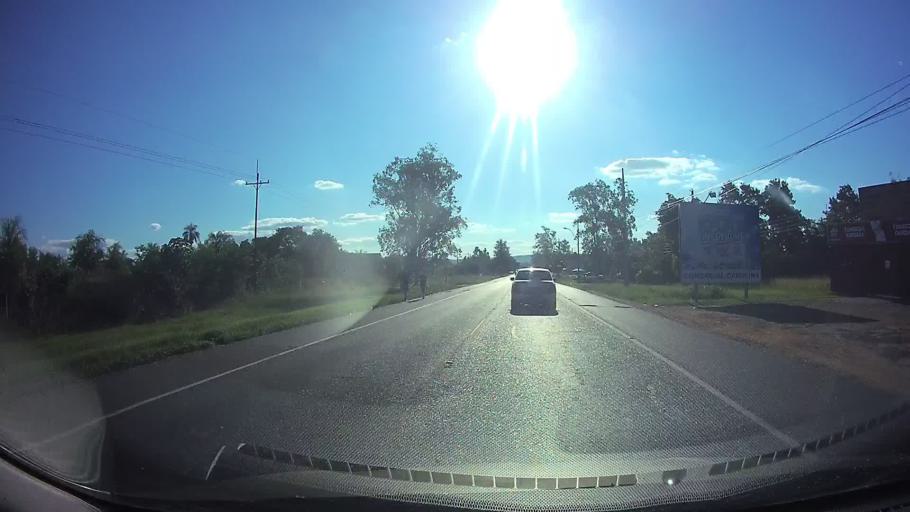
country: PY
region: Central
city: Ypacarai
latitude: -25.3786
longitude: -57.2403
